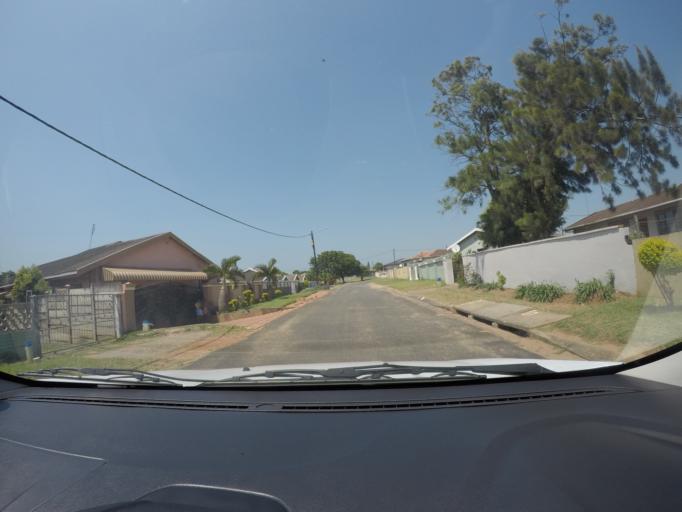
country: ZA
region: KwaZulu-Natal
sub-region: uThungulu District Municipality
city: eSikhawini
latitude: -28.8679
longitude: 31.9245
